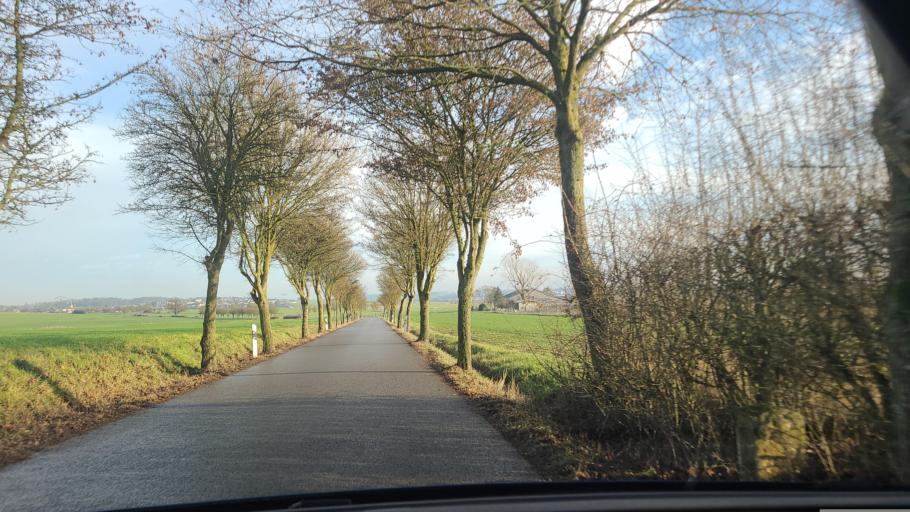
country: LU
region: Luxembourg
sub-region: Canton de Luxembourg
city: Olm
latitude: 49.6609
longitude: 5.9918
